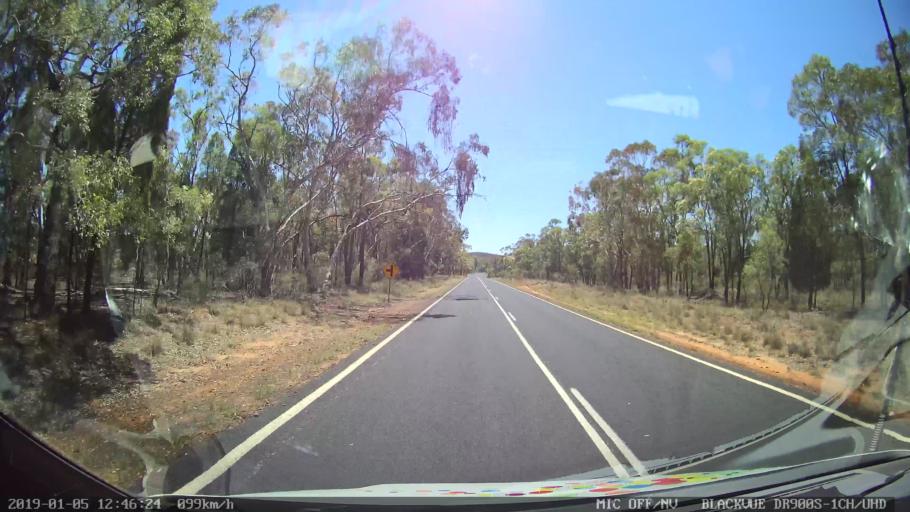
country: AU
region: New South Wales
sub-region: Warrumbungle Shire
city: Coonabarabran
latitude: -31.1184
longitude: 149.5619
